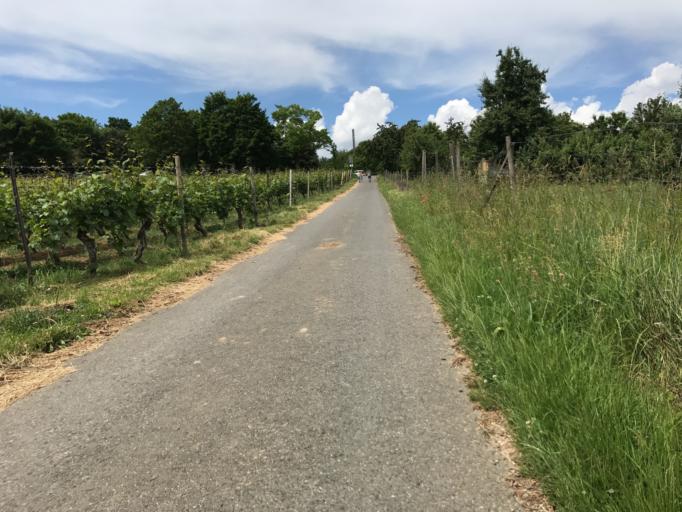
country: DE
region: Hesse
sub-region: Regierungsbezirk Darmstadt
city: Walluf
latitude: 50.0622
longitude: 8.1660
